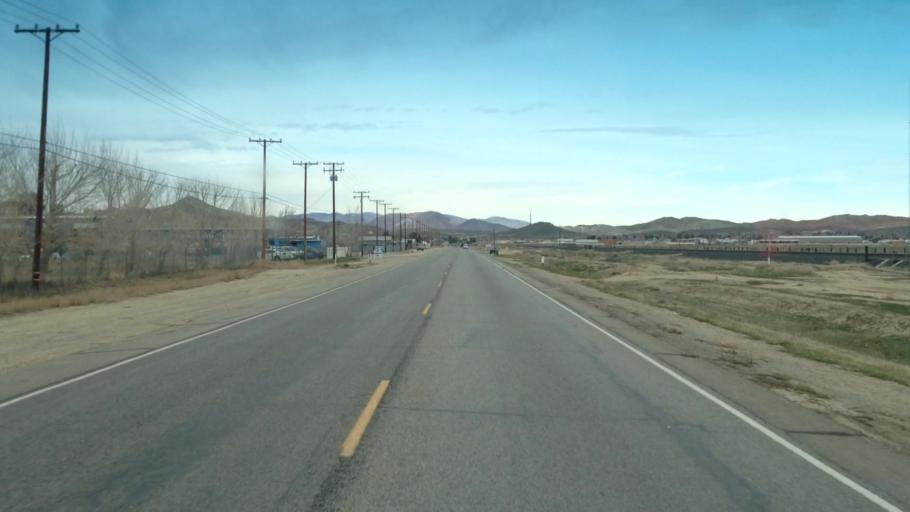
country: US
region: California
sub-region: Kern County
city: Rosamond
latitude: 34.8435
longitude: -118.1597
